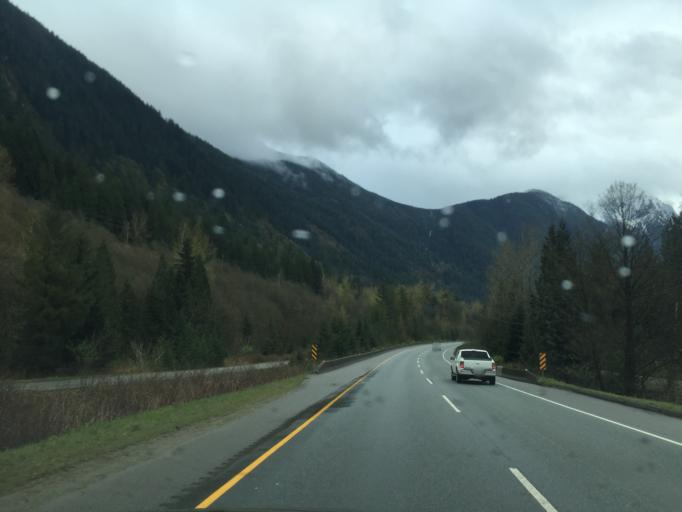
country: CA
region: British Columbia
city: Agassiz
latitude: 49.2502
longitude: -121.6800
